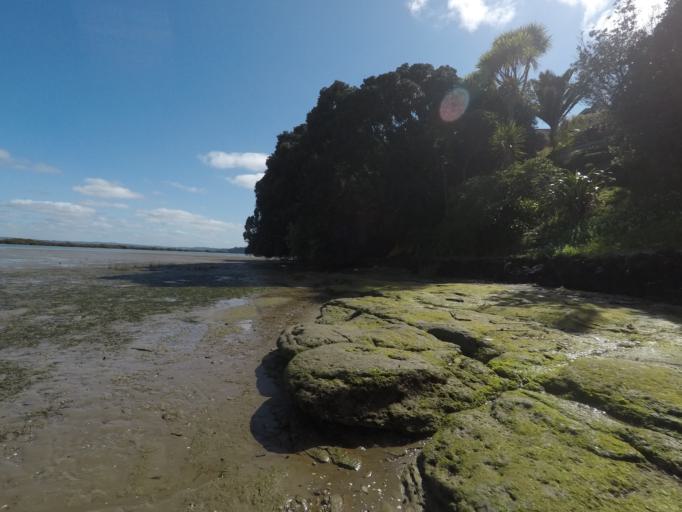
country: NZ
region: Auckland
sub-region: Auckland
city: Rosebank
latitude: -36.8534
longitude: 174.7137
